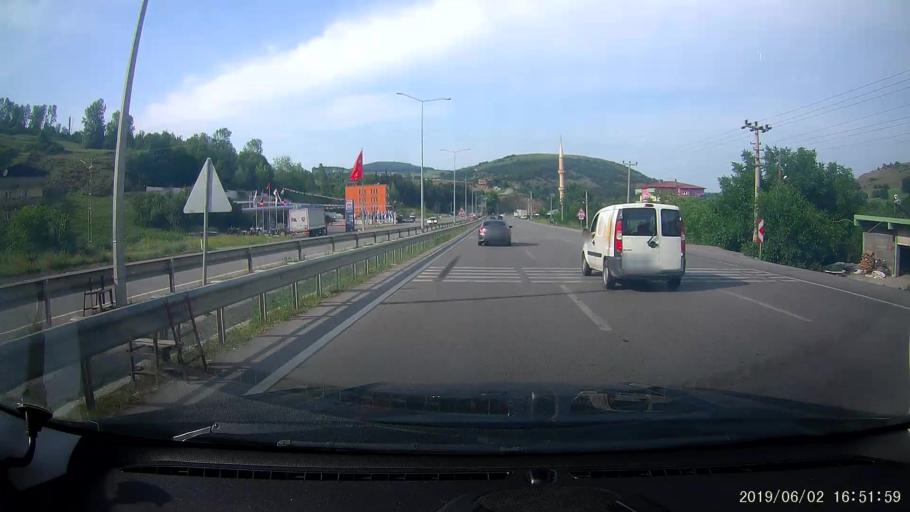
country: TR
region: Samsun
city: Samsun
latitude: 41.2814
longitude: 36.1910
